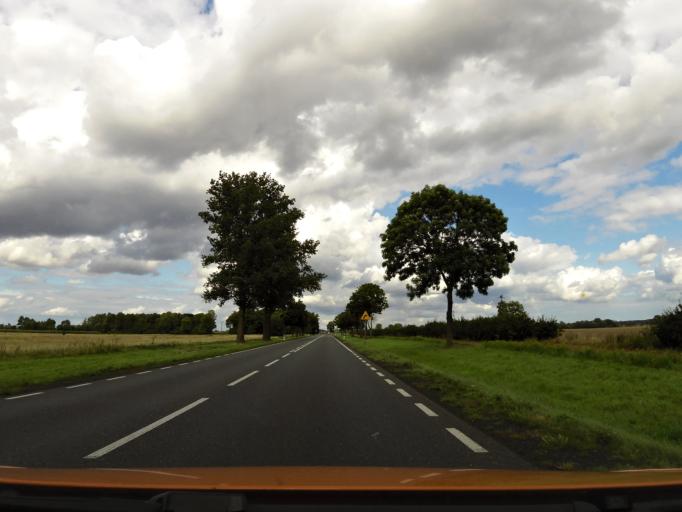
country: PL
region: West Pomeranian Voivodeship
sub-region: Powiat gryficki
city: Brojce
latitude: 53.8697
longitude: 15.3631
